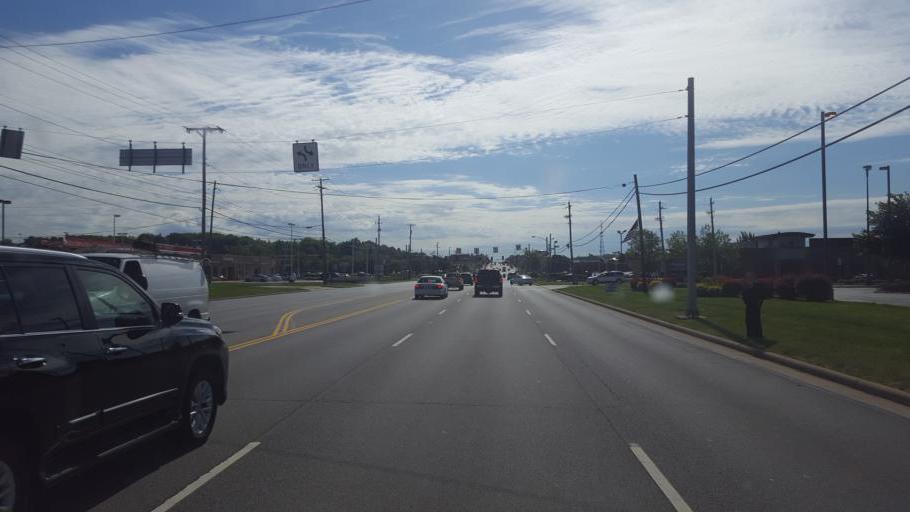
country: US
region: Ohio
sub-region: Summit County
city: Montrose-Ghent
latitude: 41.1359
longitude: -81.6445
